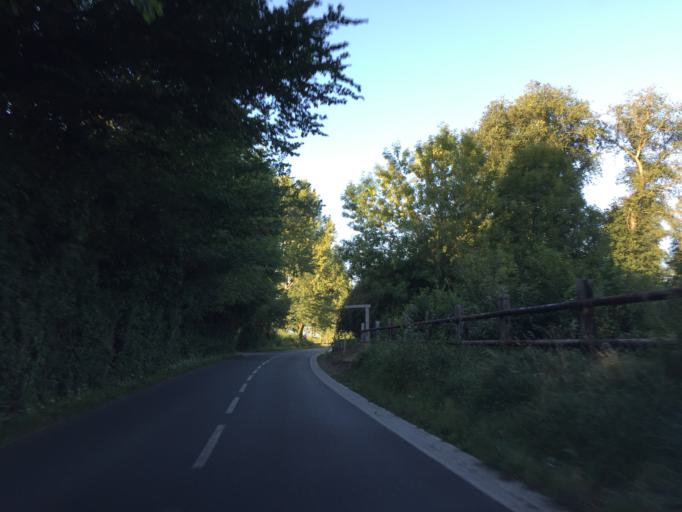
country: FR
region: Lower Normandy
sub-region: Departement du Calvados
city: Equemauville
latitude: 49.4162
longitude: 0.1909
